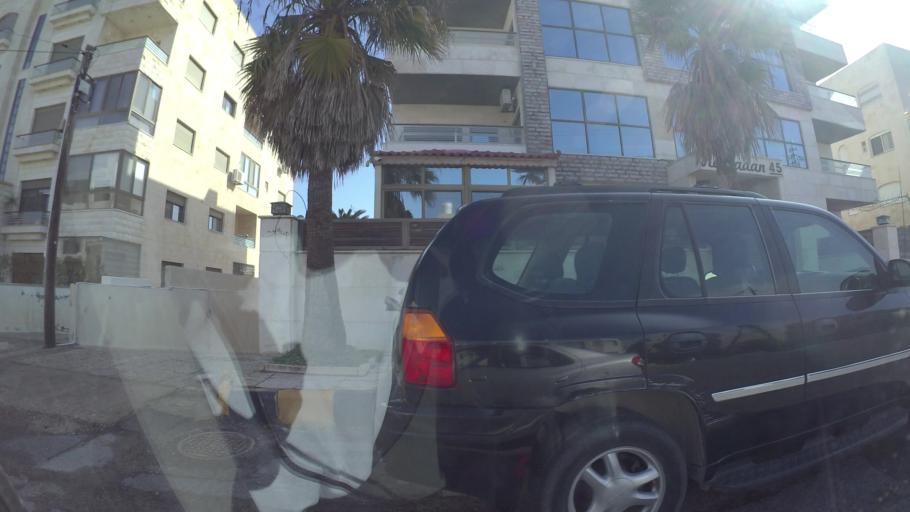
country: JO
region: Amman
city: Umm as Summaq
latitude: 31.8998
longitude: 35.8656
